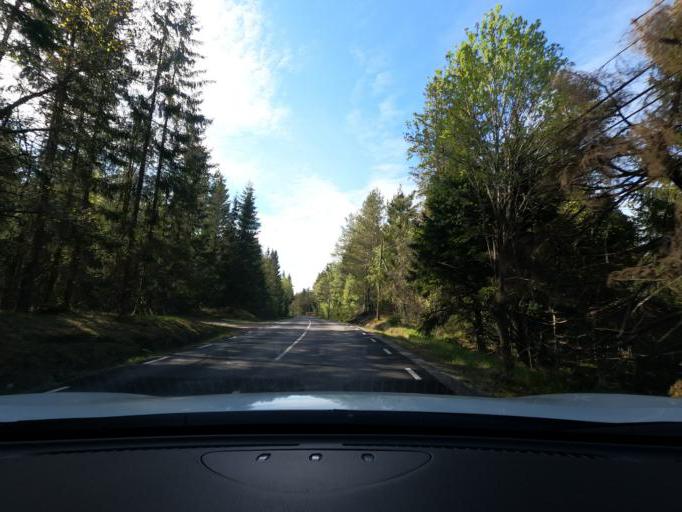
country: SE
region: Vaestra Goetaland
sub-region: Harryda Kommun
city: Landvetter
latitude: 57.6291
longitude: 12.2740
